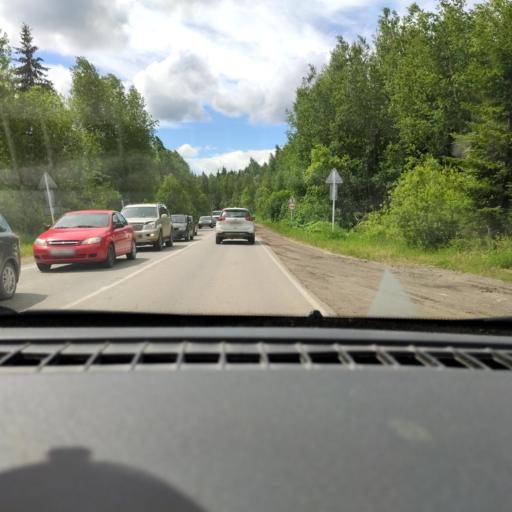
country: RU
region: Perm
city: Overyata
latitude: 58.1130
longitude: 55.8325
